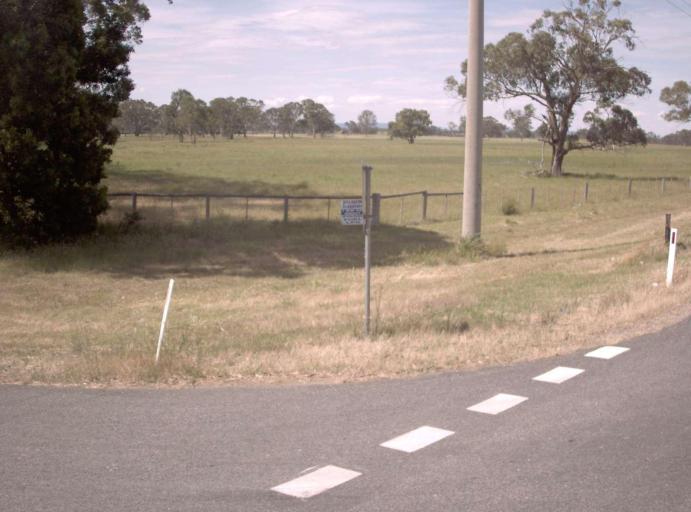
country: AU
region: Victoria
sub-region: East Gippsland
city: Bairnsdale
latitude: -37.9084
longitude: 147.3215
